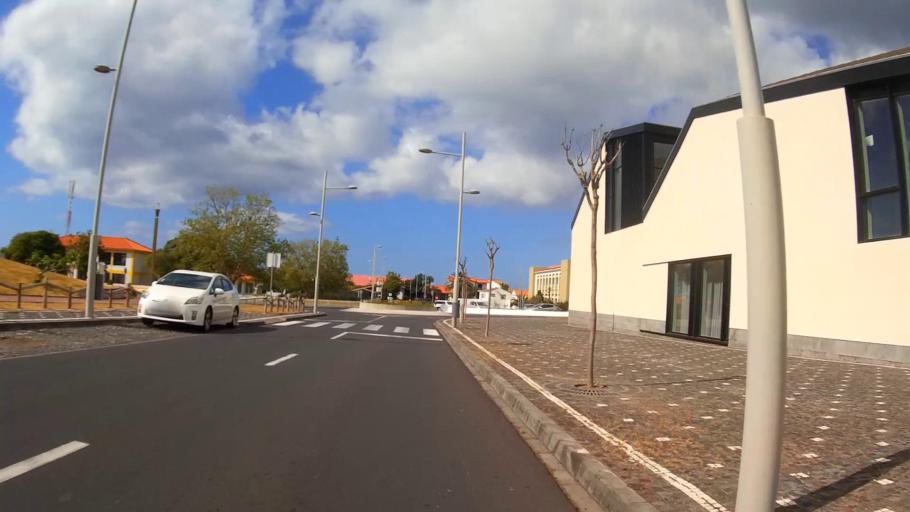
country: PT
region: Azores
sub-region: Madalena
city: Madalena
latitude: 38.5336
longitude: -28.5254
